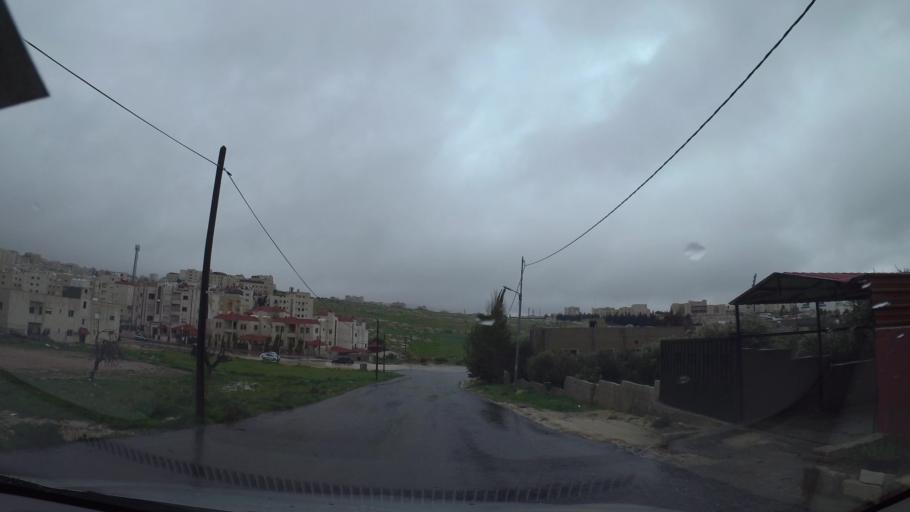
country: JO
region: Amman
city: Al Jubayhah
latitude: 32.0381
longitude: 35.8940
